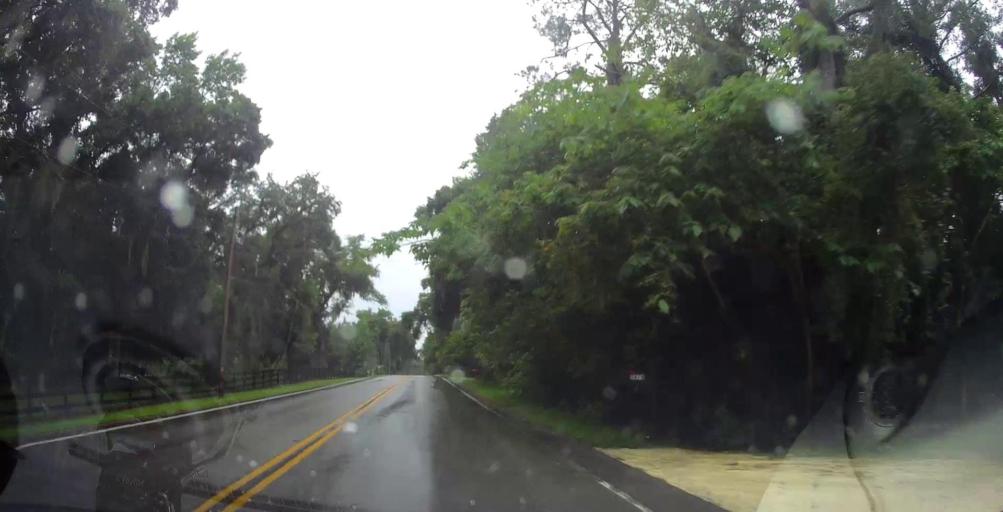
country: US
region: Florida
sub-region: Marion County
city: Citra
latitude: 29.3459
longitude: -82.2169
